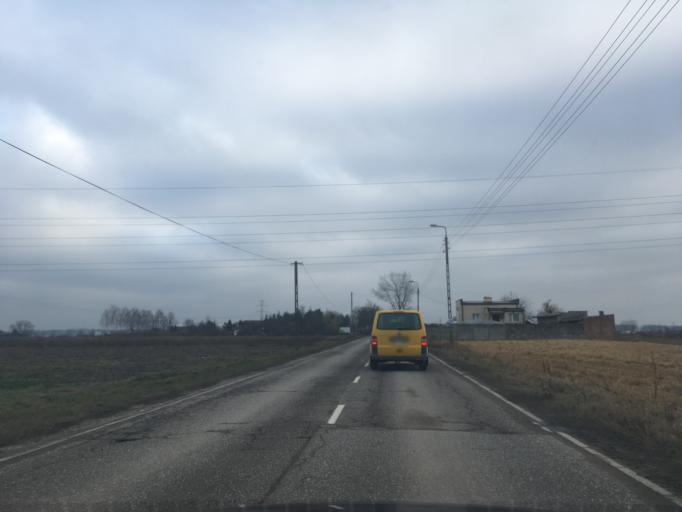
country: PL
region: Masovian Voivodeship
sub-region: Powiat piaseczynski
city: Lesznowola
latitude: 52.0901
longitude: 20.9709
